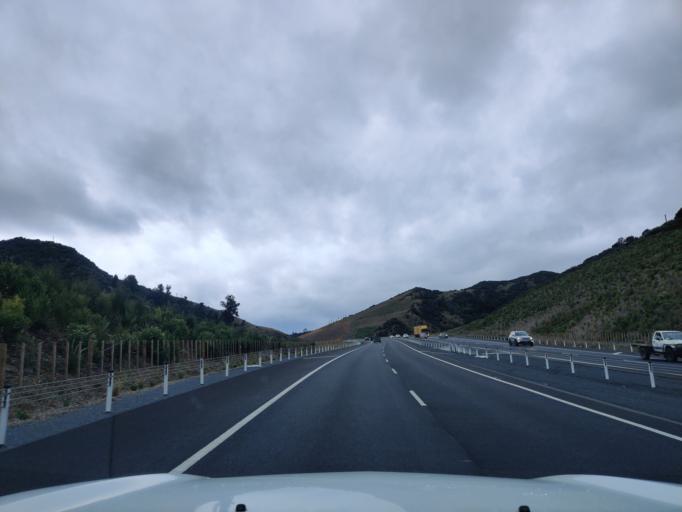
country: NZ
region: Waikato
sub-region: Waikato District
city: Ngaruawahia
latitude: -37.5744
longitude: 175.1868
